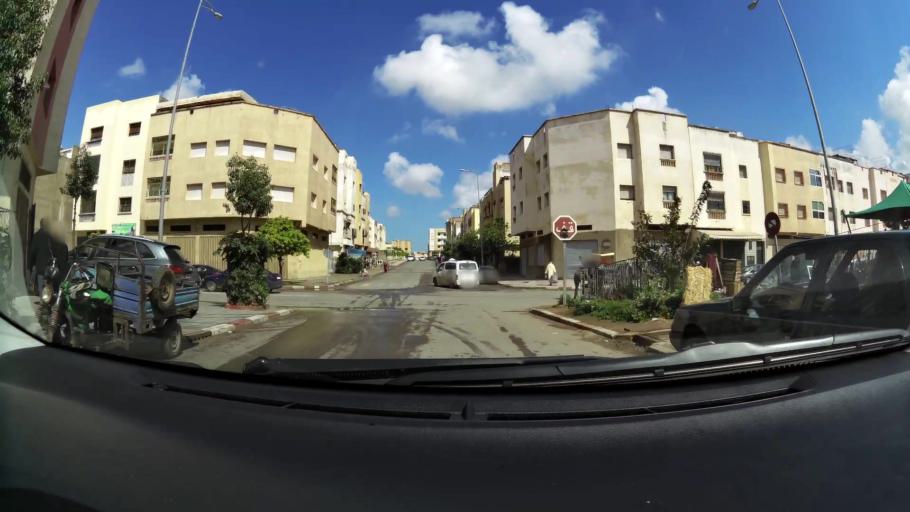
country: MA
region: Grand Casablanca
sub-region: Mediouna
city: Tit Mellil
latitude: 33.5494
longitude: -7.4842
